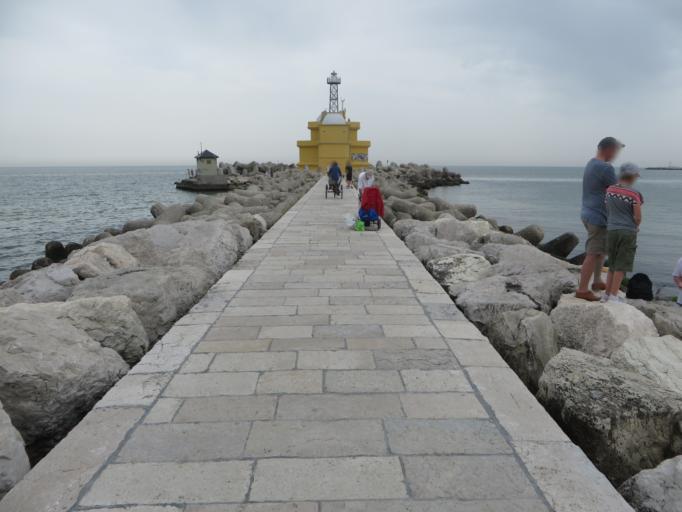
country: IT
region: Veneto
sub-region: Provincia di Venezia
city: Ca' Savio
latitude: 45.4235
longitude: 12.4356
